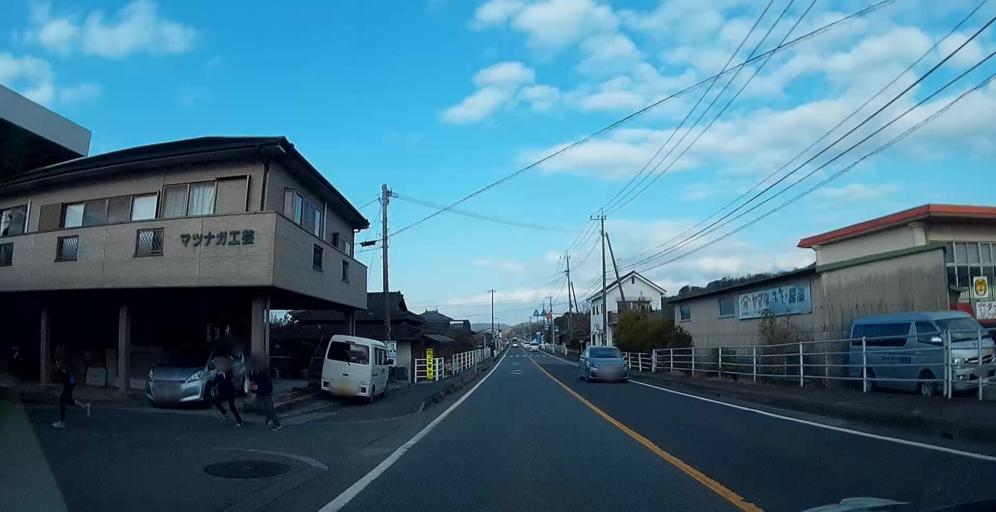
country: JP
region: Kumamoto
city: Matsubase
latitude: 32.5590
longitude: 130.6829
